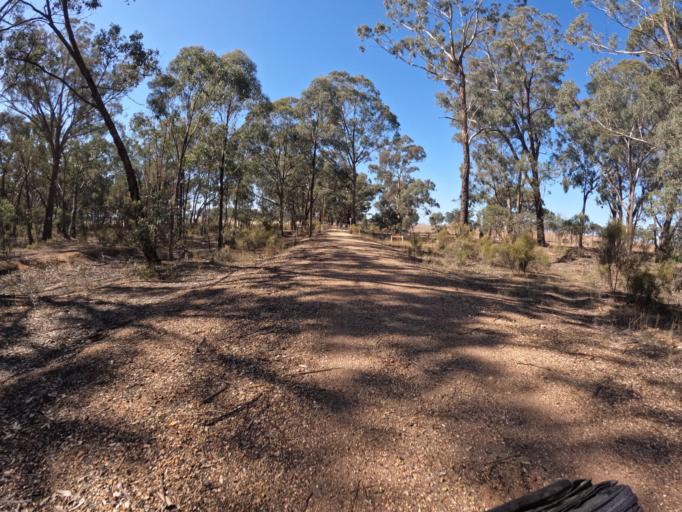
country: AU
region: Victoria
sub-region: Greater Bendigo
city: Kennington
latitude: -36.8187
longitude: 144.5697
